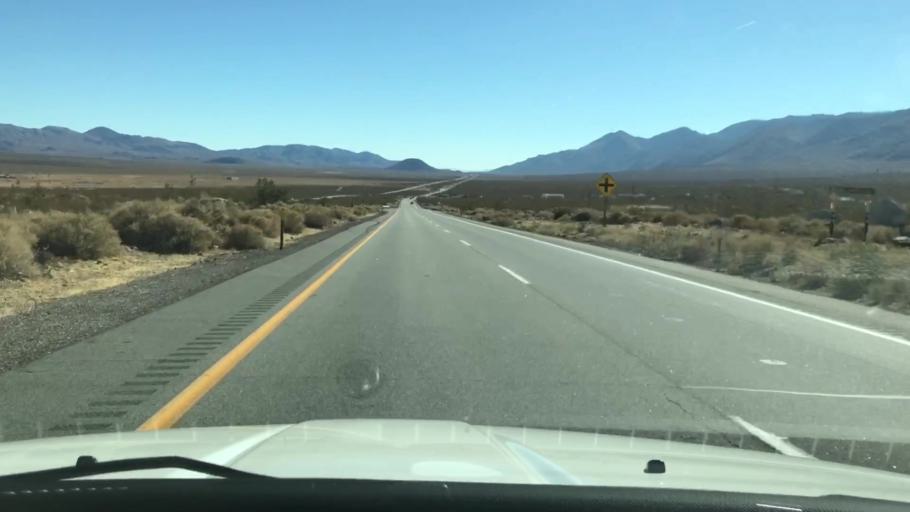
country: US
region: California
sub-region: Kern County
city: Inyokern
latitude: 36.0960
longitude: -117.9648
